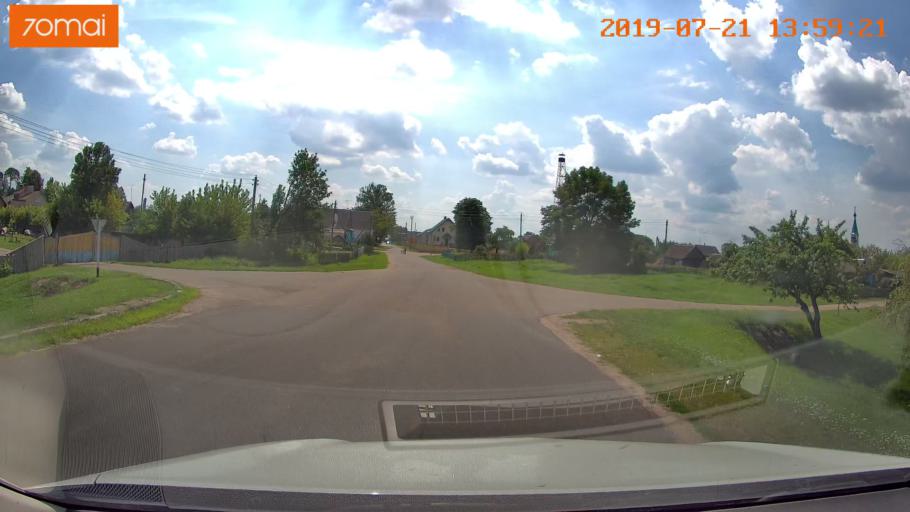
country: BY
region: Grodnenskaya
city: Lyubcha
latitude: 53.7542
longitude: 26.0643
